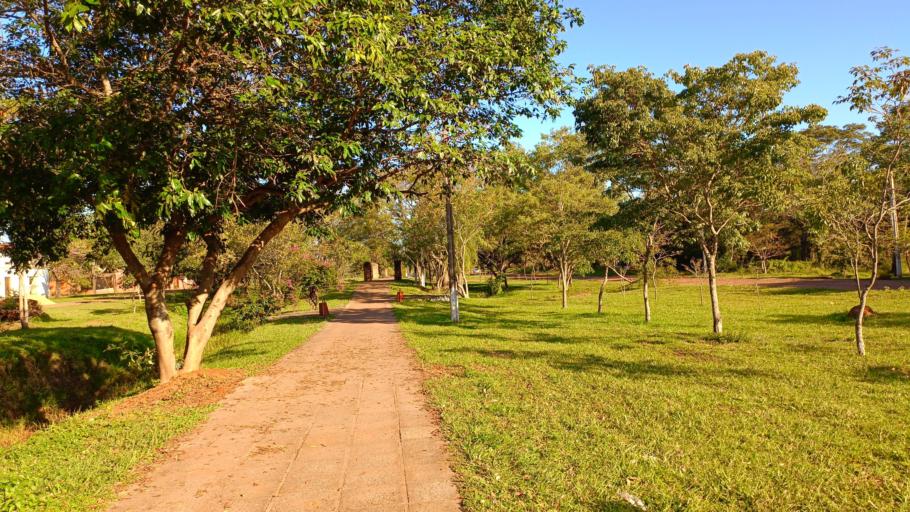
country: PY
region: Itapua
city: Carmen del Parana
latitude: -27.1648
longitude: -56.2400
